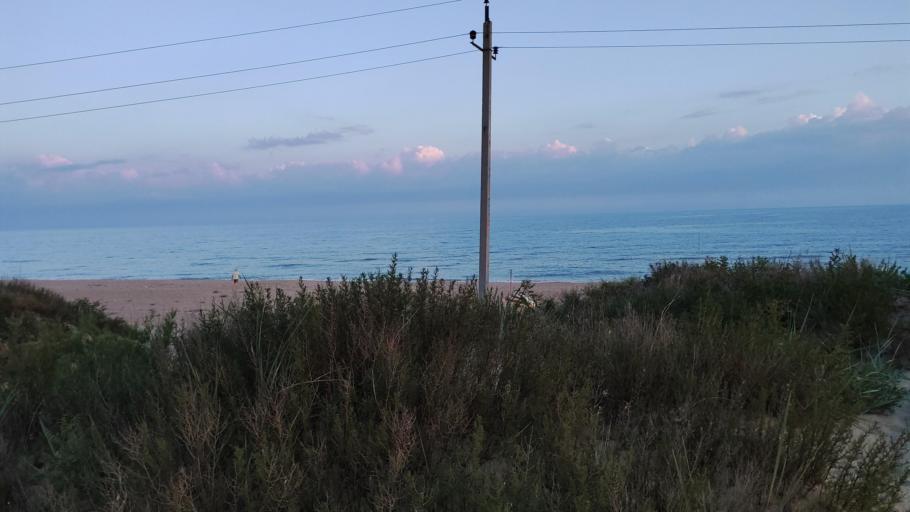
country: RU
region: Krasnodarskiy
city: Blagovetschenskaya
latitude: 45.0689
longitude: 37.0254
